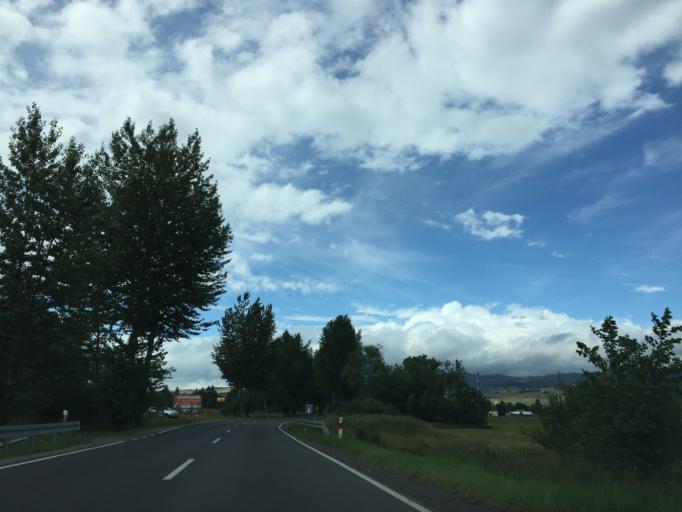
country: PL
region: Lesser Poland Voivodeship
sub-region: Powiat nowotarski
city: Waksmund
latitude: 49.4696
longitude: 20.0573
